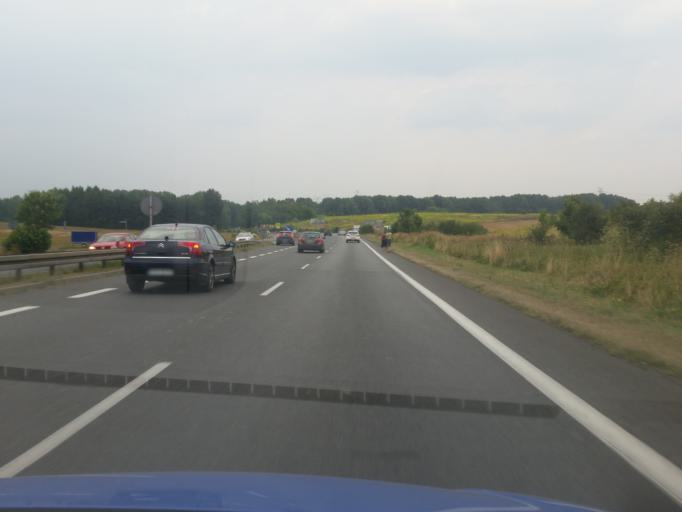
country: PL
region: Silesian Voivodeship
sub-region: Powiat bedzinski
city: Siewierz
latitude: 50.4429
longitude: 19.2214
